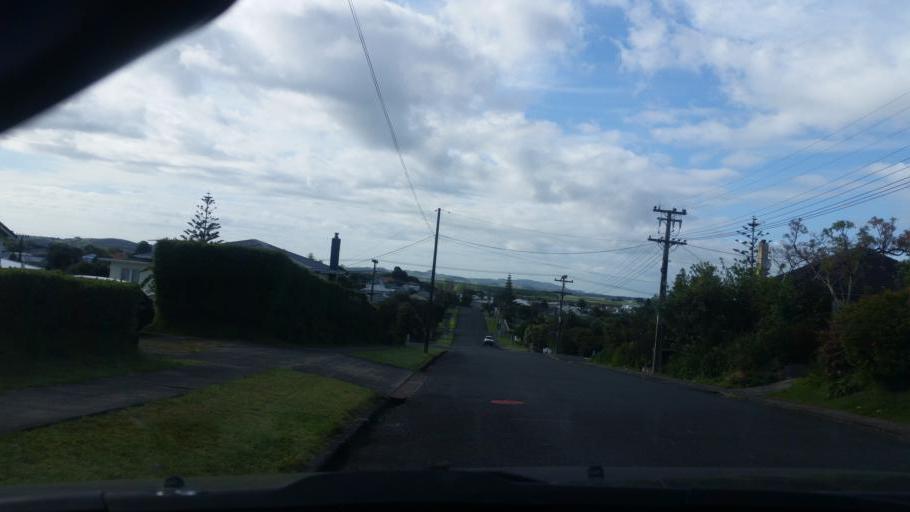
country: NZ
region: Northland
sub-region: Kaipara District
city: Dargaville
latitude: -35.9341
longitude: 173.8685
